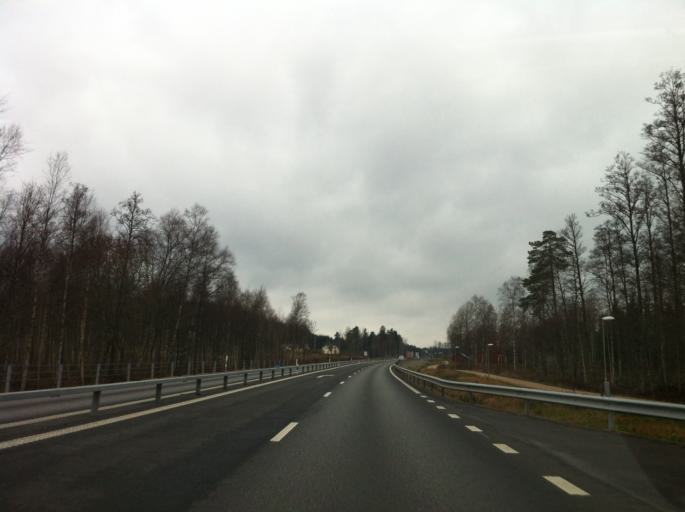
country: SE
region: Joenkoeping
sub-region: Vetlanda Kommun
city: Vetlanda
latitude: 57.4280
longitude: 15.1500
